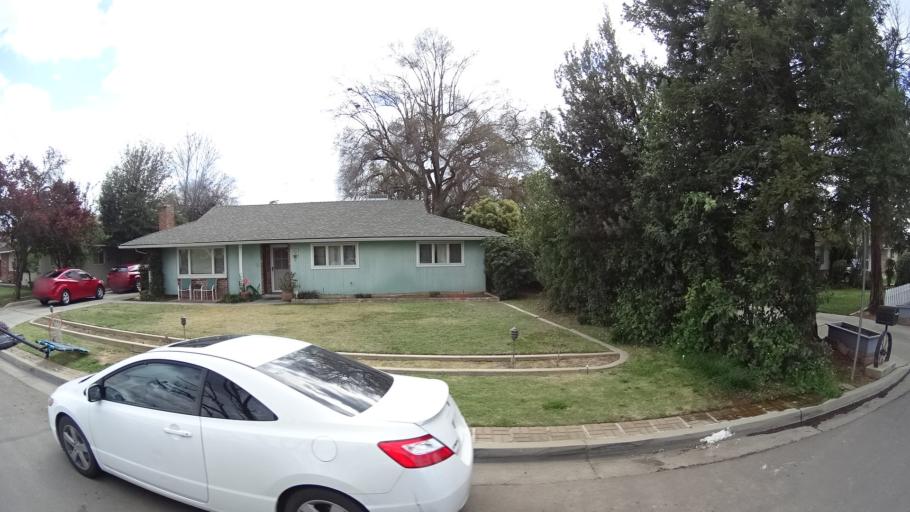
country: US
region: California
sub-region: Fresno County
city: Clovis
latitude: 36.8186
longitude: -119.7648
